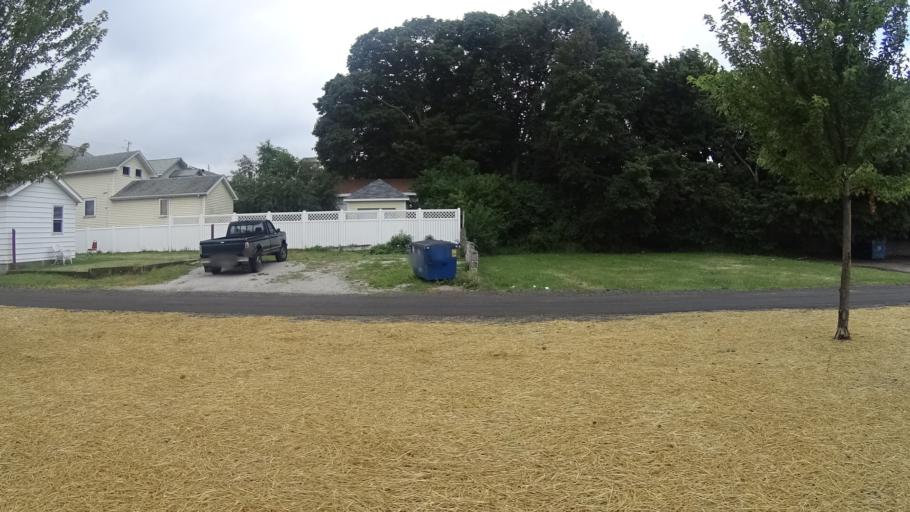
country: US
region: Ohio
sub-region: Erie County
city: Sandusky
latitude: 41.4562
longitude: -82.7041
